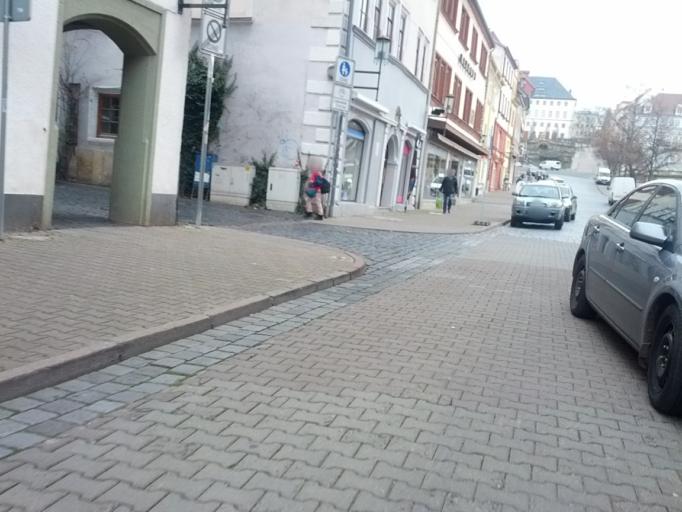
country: DE
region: Thuringia
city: Gotha
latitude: 50.9490
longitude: 10.7019
